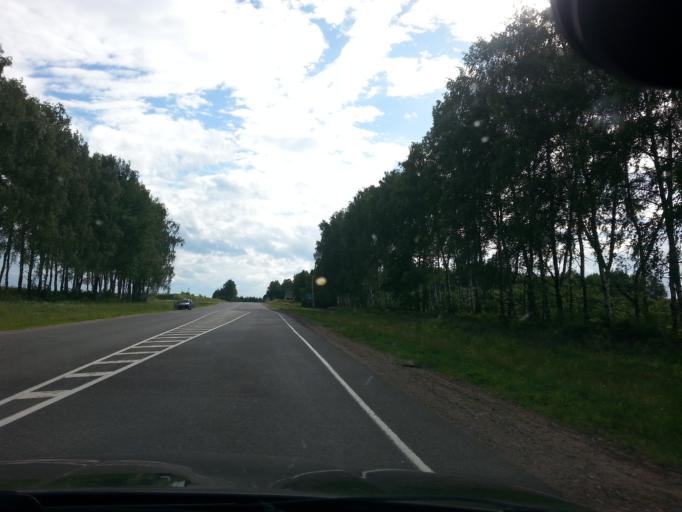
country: BY
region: Grodnenskaya
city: Astravyets
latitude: 54.7821
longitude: 26.0568
